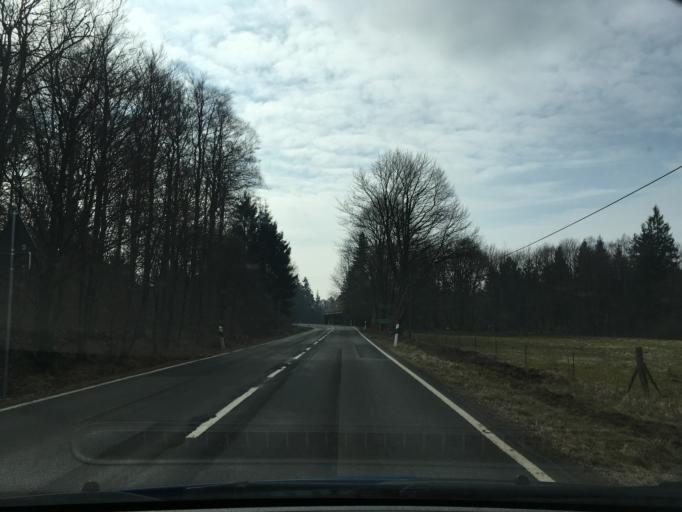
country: DE
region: Lower Saxony
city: Heinade
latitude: 51.7655
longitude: 9.5619
